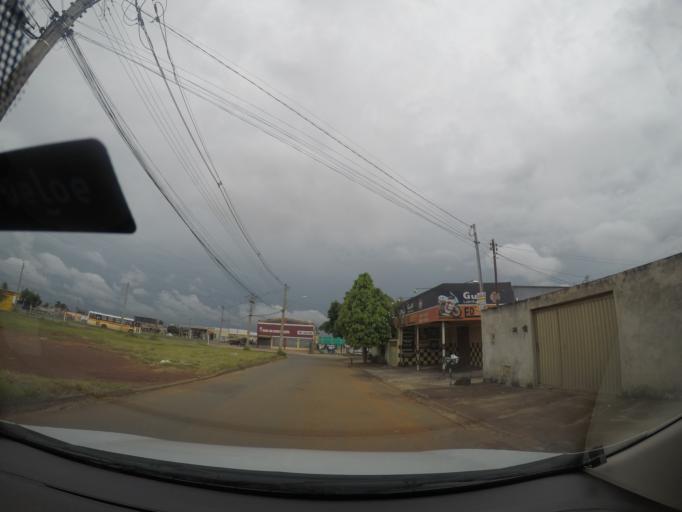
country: BR
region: Goias
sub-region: Goiania
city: Goiania
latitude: -16.7345
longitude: -49.3470
